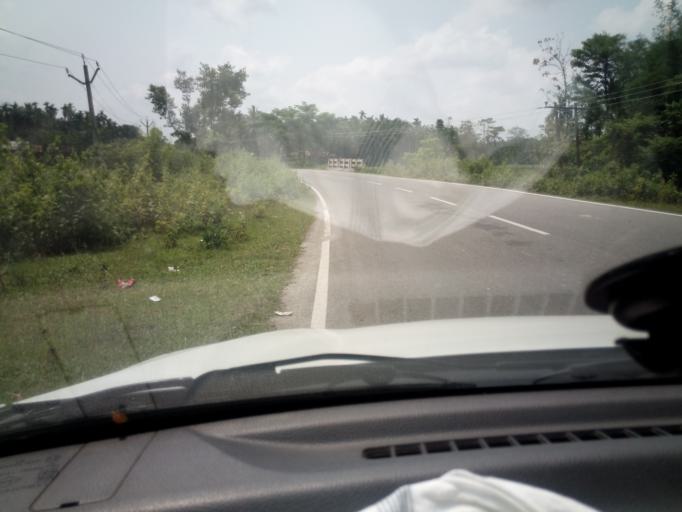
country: IN
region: Assam
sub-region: Udalguri
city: Udalguri
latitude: 26.7210
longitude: 92.1939
